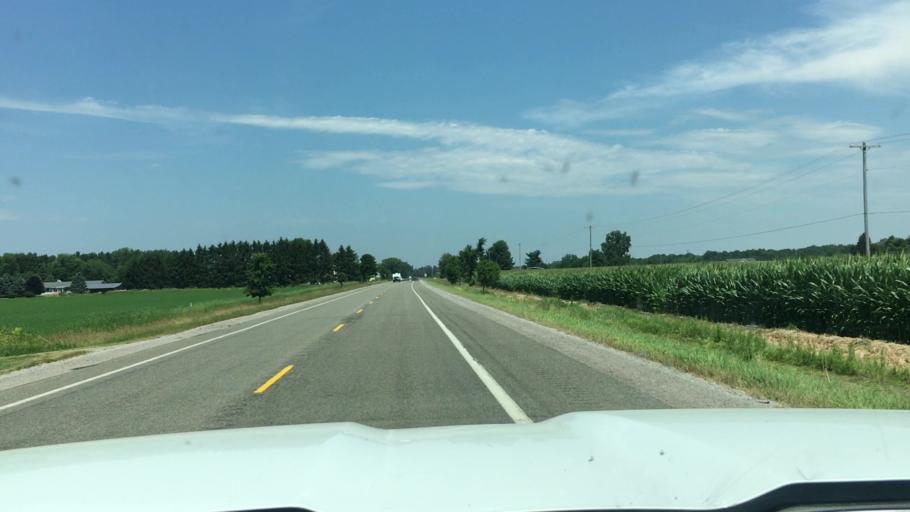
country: US
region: Michigan
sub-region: Saginaw County
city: Chesaning
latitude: 43.1972
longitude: -84.1693
